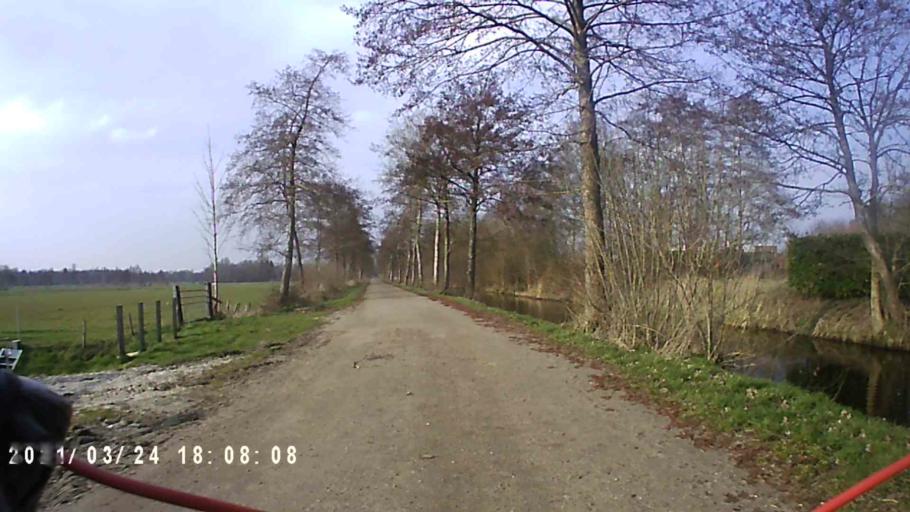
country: NL
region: Groningen
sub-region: Gemeente Leek
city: Leek
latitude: 53.1483
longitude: 6.3631
